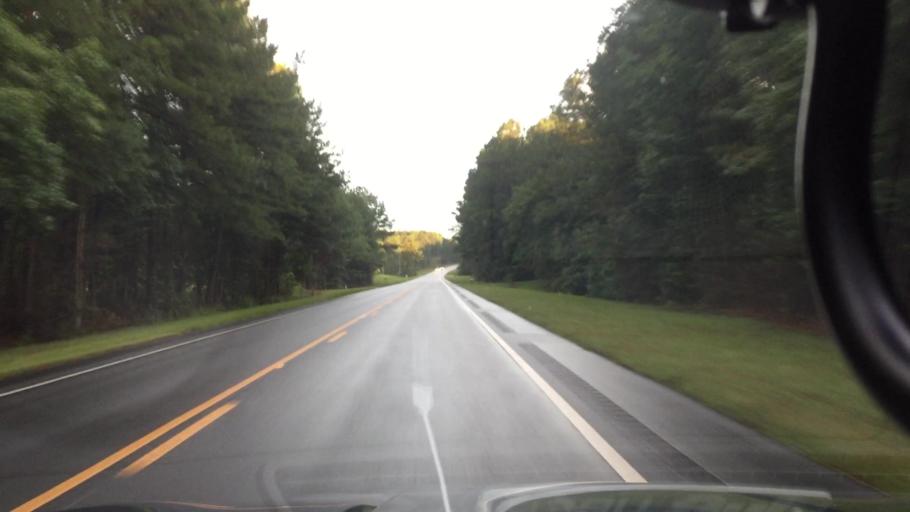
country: US
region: Alabama
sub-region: Coffee County
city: New Brockton
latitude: 31.5576
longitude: -85.9225
